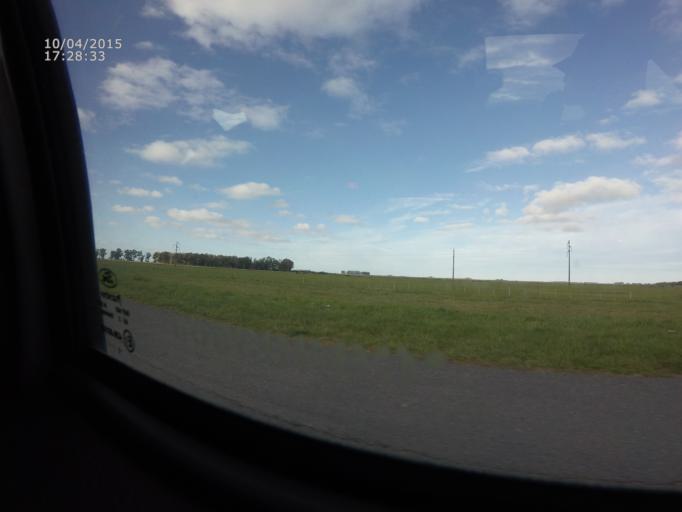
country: AR
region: Buenos Aires
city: Maipu
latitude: -37.0230
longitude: -57.8492
